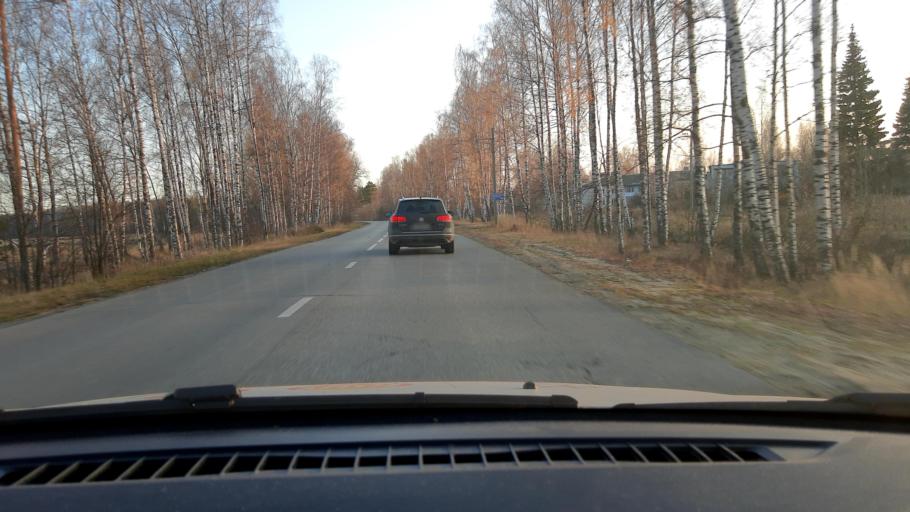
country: RU
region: Nizjnij Novgorod
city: Volodarsk
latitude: 56.2568
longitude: 43.1698
